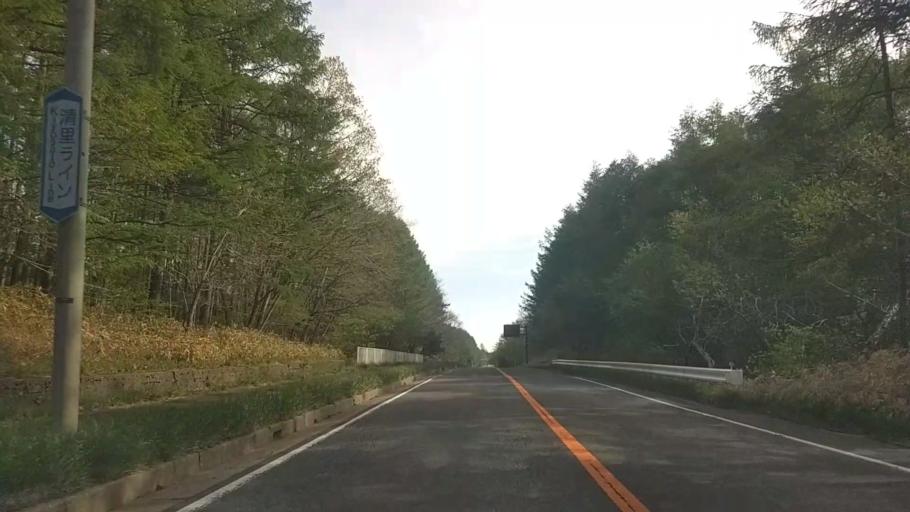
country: JP
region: Yamanashi
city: Nirasaki
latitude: 35.9376
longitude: 138.4484
